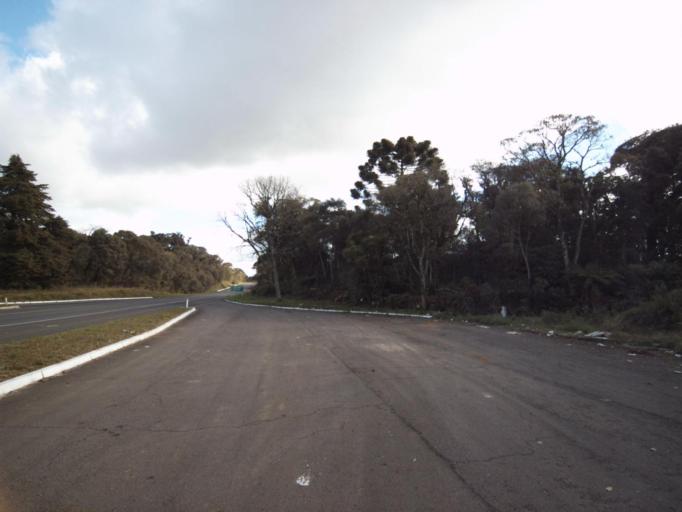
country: BR
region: Santa Catarina
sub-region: Concordia
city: Concordia
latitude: -26.9798
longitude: -51.8064
